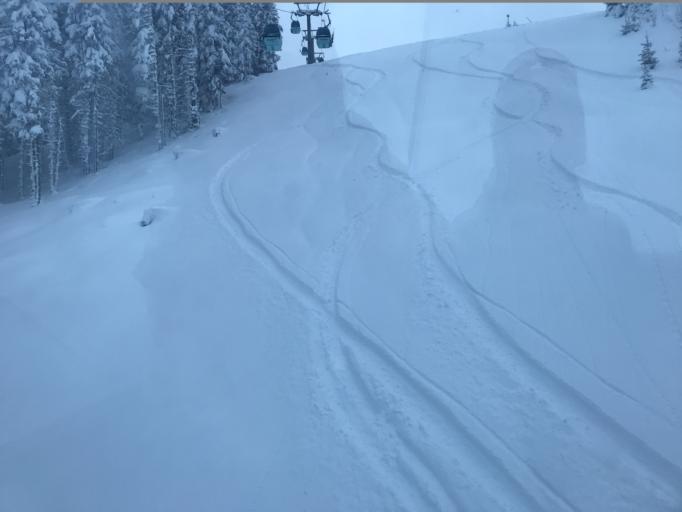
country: AT
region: Salzburg
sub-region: Politischer Bezirk Zell am See
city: Kaprun
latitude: 47.3141
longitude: 12.7528
